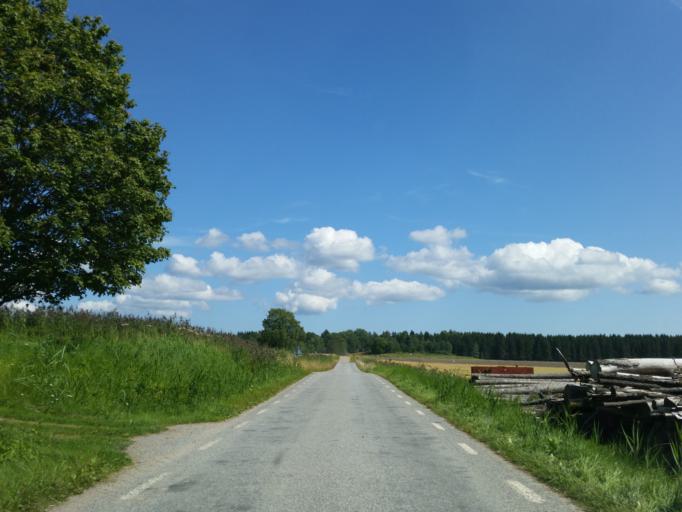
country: SE
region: Stockholm
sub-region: Sodertalje Kommun
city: Pershagen
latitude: 59.0452
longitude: 17.6704
